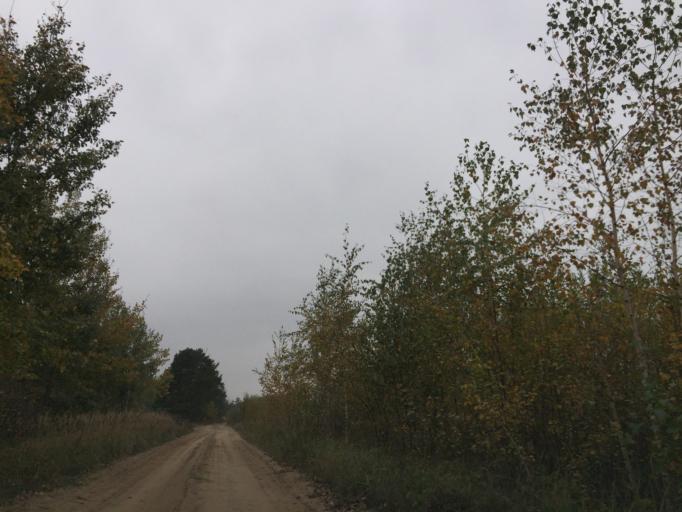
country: LV
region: Dobeles Rajons
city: Dobele
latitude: 56.6739
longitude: 23.4592
